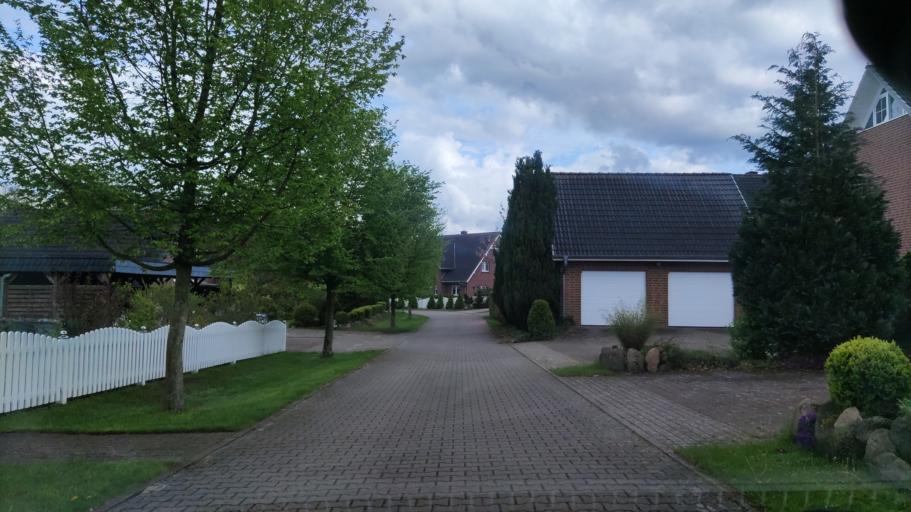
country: DE
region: Lower Saxony
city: Oldendorf
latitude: 53.1521
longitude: 10.2135
